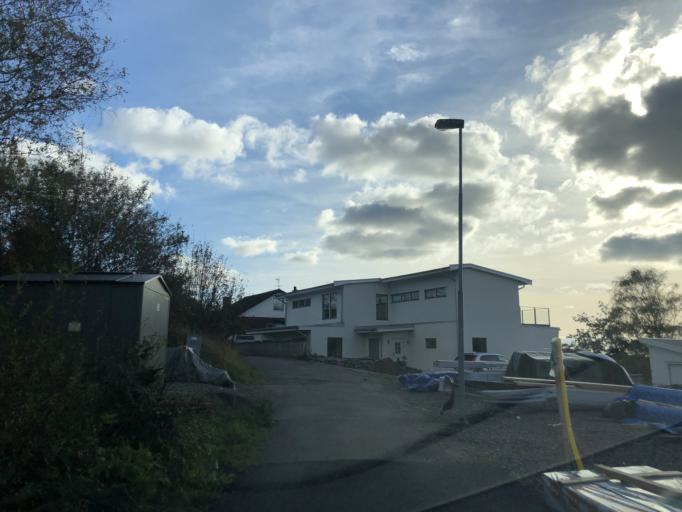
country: SE
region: Vaestra Goetaland
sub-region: Goteborg
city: Billdal
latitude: 57.6270
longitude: 11.9406
